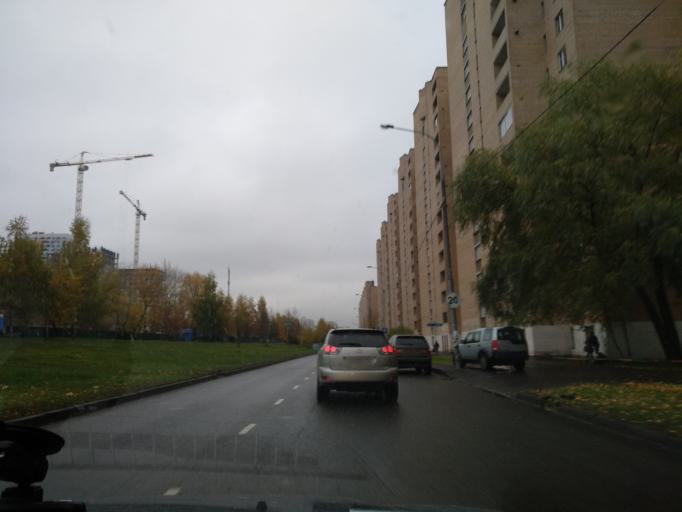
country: RU
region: Moscow
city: Otradnoye
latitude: 55.8726
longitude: 37.5993
